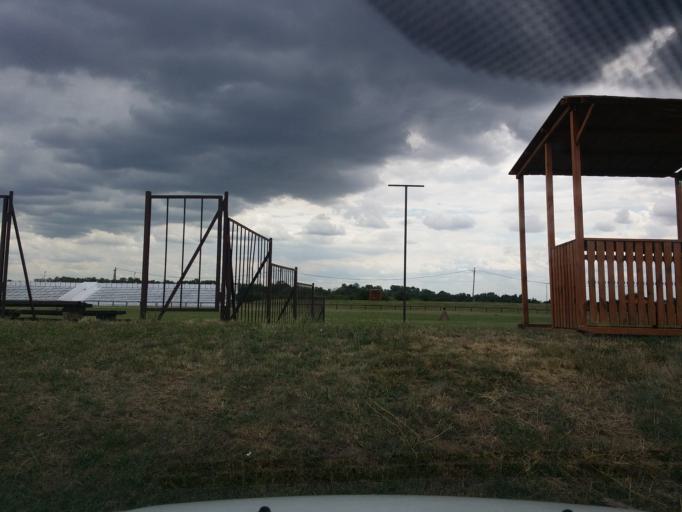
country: HU
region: Hajdu-Bihar
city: Hortobagy
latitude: 47.5948
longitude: 21.1482
